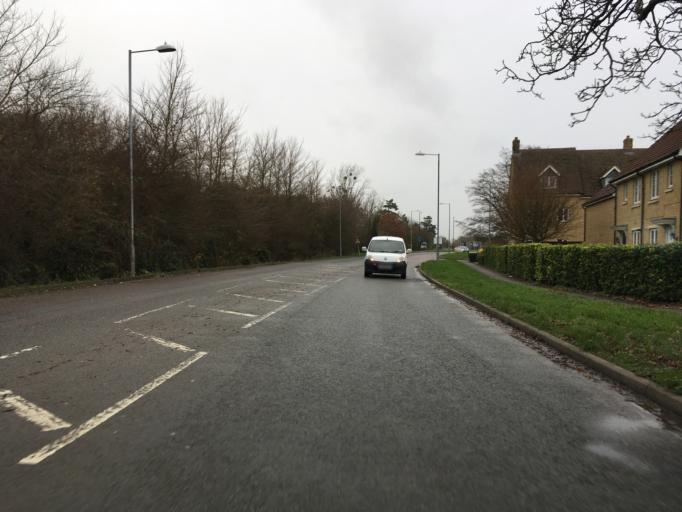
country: GB
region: England
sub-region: Wiltshire
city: Malmesbury
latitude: 51.5959
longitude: -2.1036
